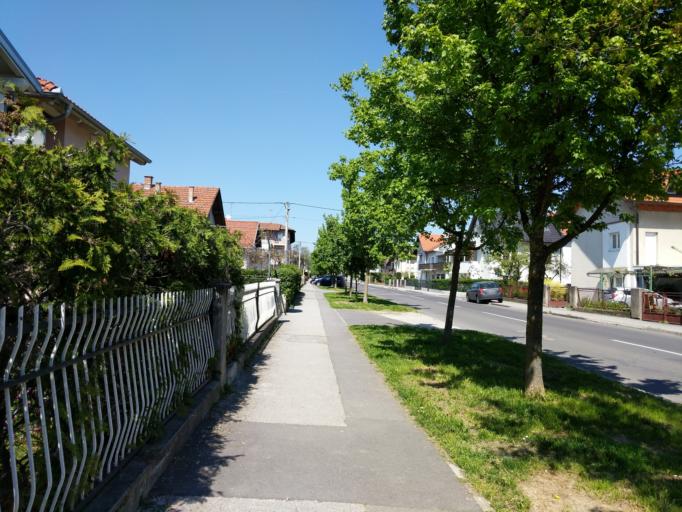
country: HR
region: Grad Zagreb
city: Dubrava
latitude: 45.8303
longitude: 16.0819
